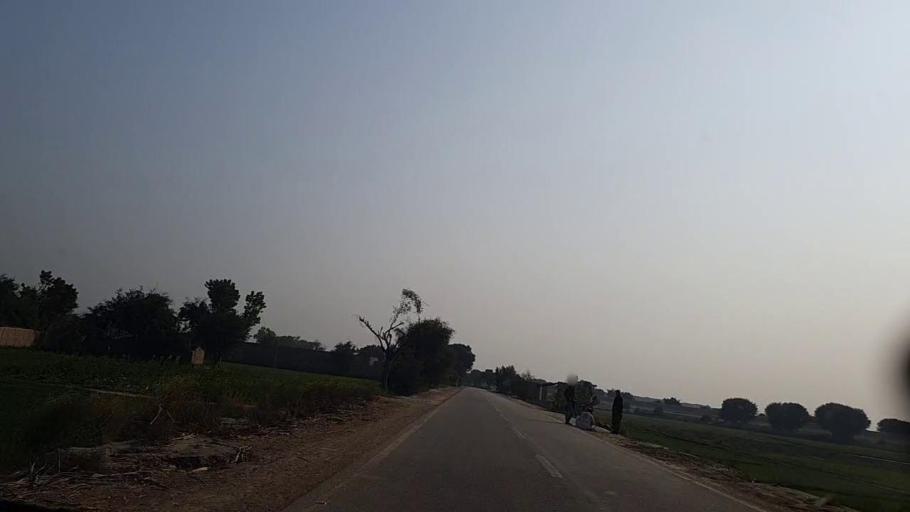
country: PK
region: Sindh
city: Sann
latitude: 26.1729
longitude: 68.1071
